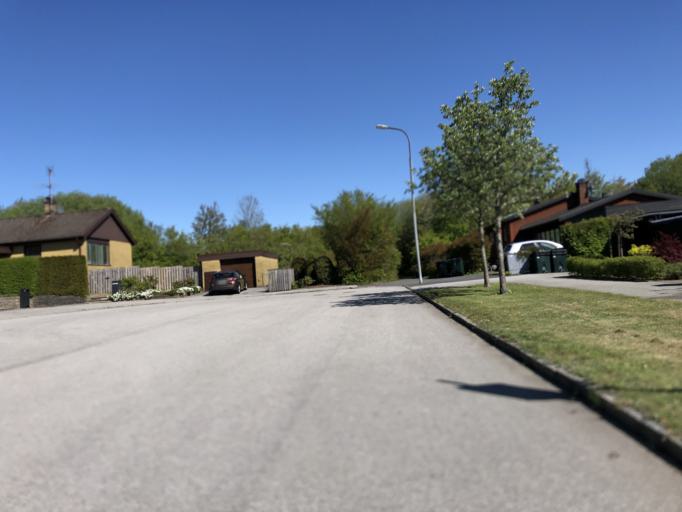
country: SE
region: Skane
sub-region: Lunds Kommun
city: Lund
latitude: 55.7067
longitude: 13.2260
